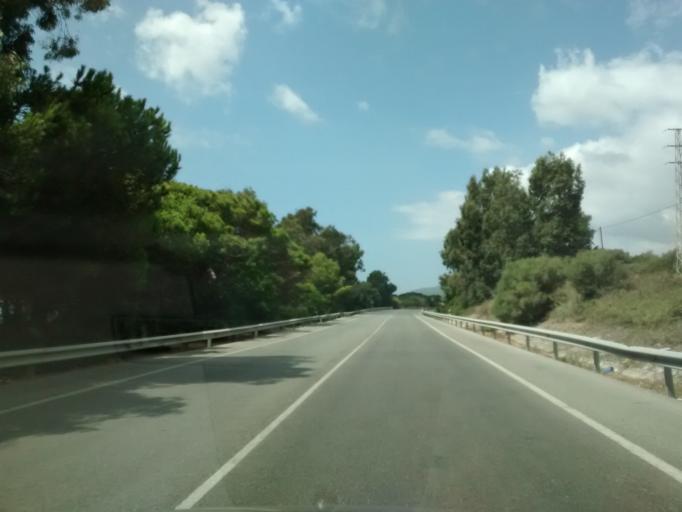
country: ES
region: Andalusia
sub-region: Provincia de Cadiz
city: Tarifa
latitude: 36.0567
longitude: -5.6610
